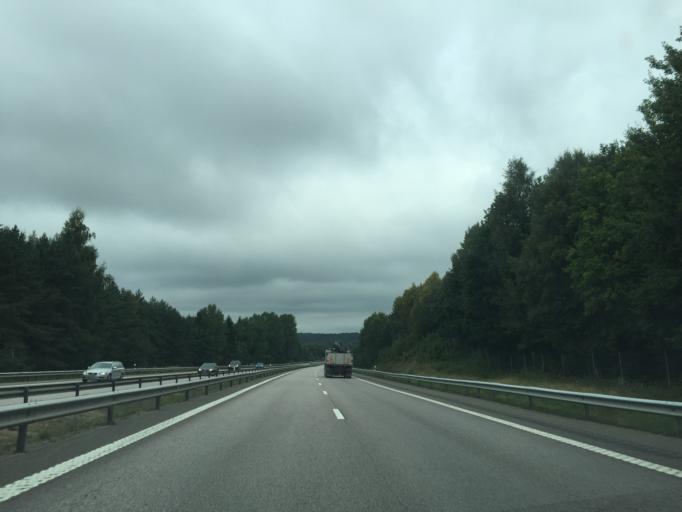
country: SE
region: Halland
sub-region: Kungsbacka Kommun
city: Fjaeras kyrkby
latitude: 57.4052
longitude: 12.1786
